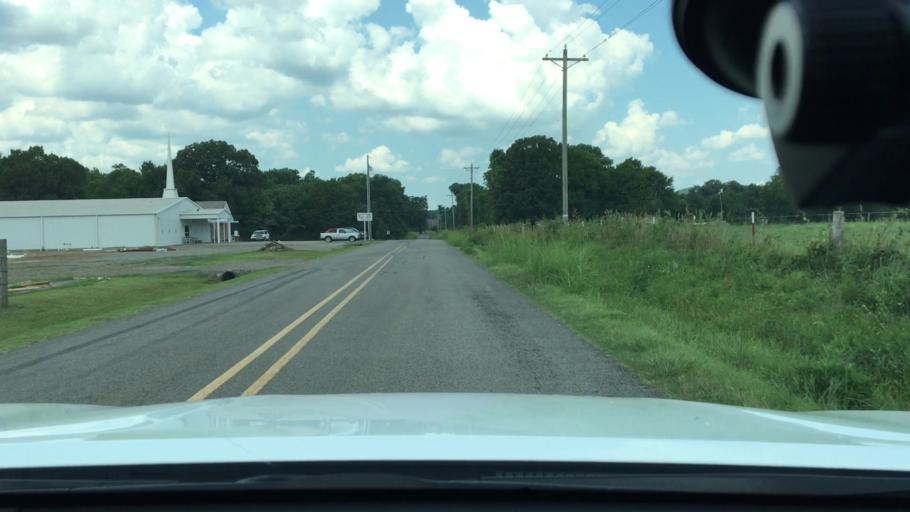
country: US
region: Arkansas
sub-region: Logan County
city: Paris
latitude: 35.2690
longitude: -93.6590
